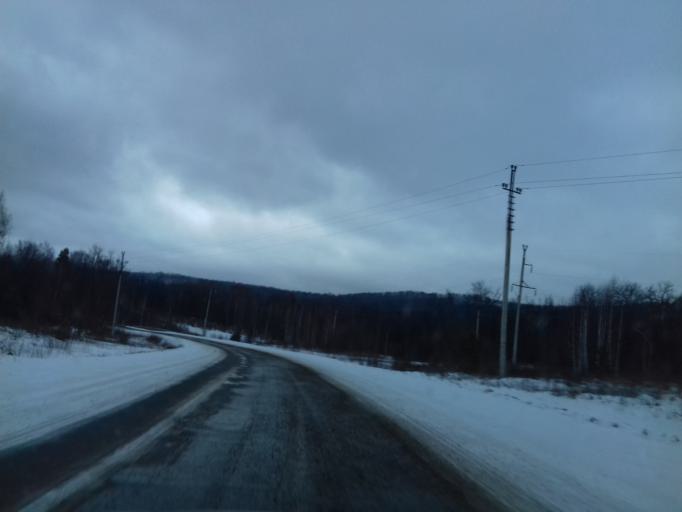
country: RU
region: Bashkortostan
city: Starosubkhangulovo
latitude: 53.2154
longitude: 57.4389
